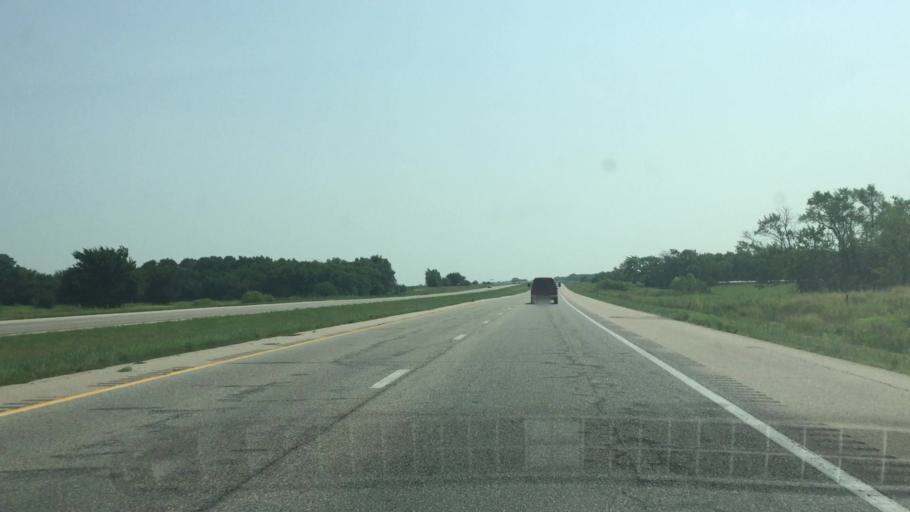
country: US
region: Kansas
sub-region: Osage County
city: Lyndon
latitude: 38.4266
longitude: -95.7696
